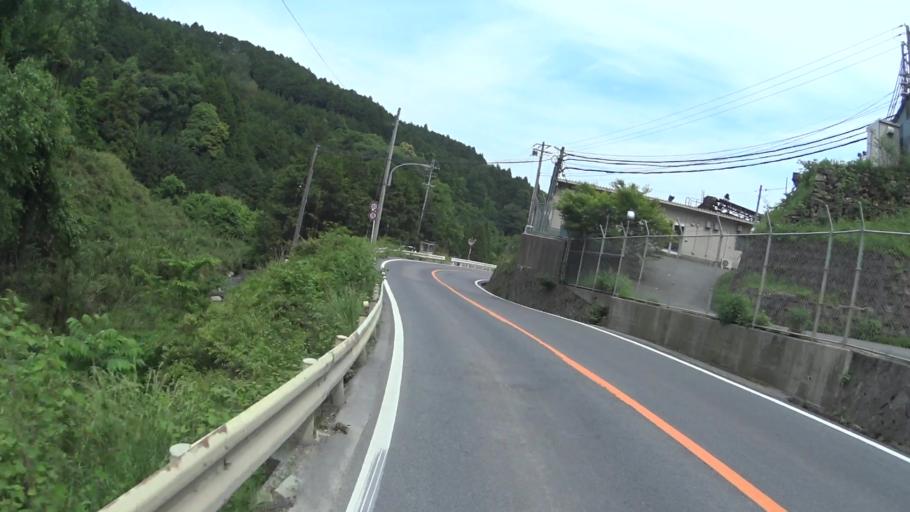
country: JP
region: Shiga Prefecture
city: Kitahama
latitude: 35.1637
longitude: 135.8604
